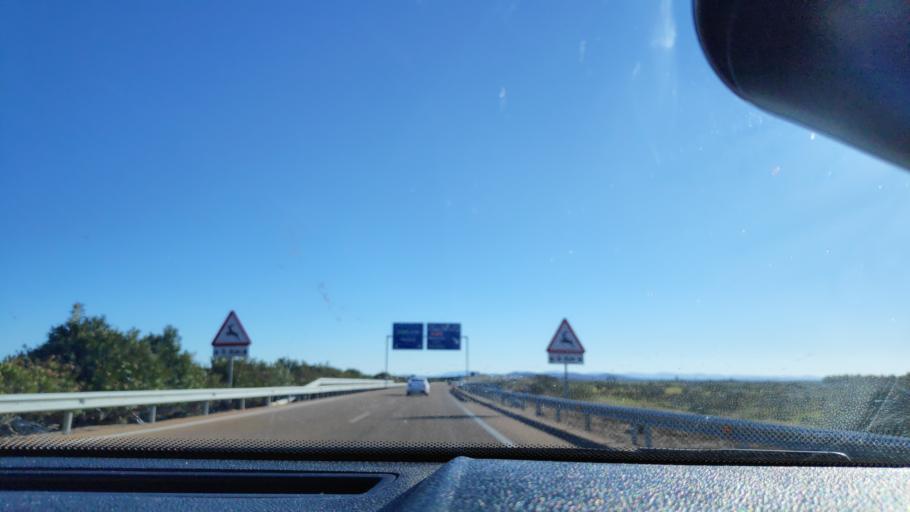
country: ES
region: Extremadura
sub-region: Provincia de Badajoz
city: Puebla de Sancho Perez
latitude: 38.4081
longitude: -6.3416
